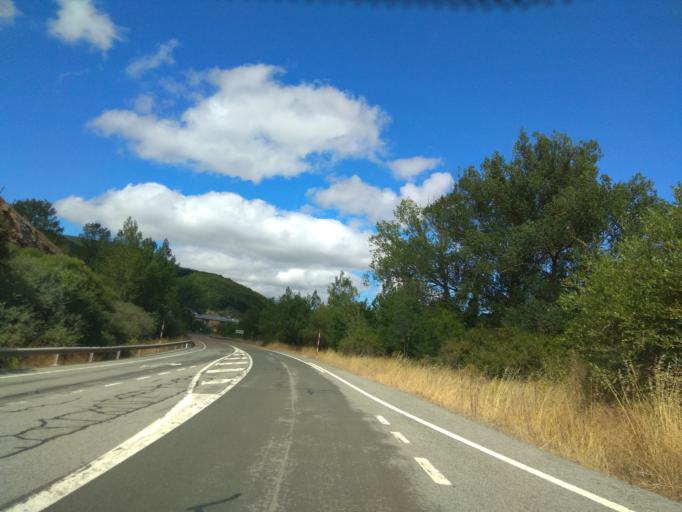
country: ES
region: Cantabria
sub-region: Provincia de Cantabria
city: Villaescusa
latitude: 42.9501
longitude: -4.1373
